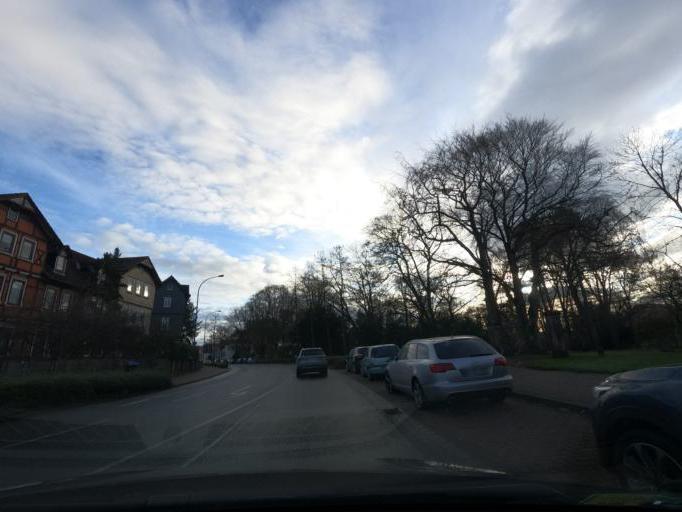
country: DE
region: Lower Saxony
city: Wolfenbuettel
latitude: 52.1667
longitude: 10.5428
